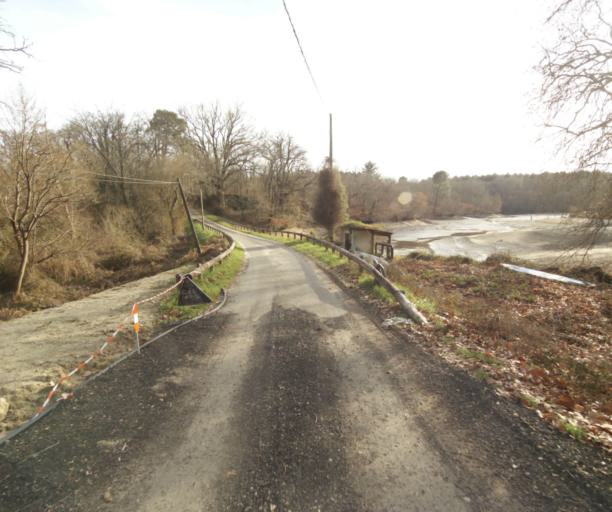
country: FR
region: Aquitaine
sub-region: Departement des Landes
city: Gabarret
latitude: 44.0092
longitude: 0.0256
